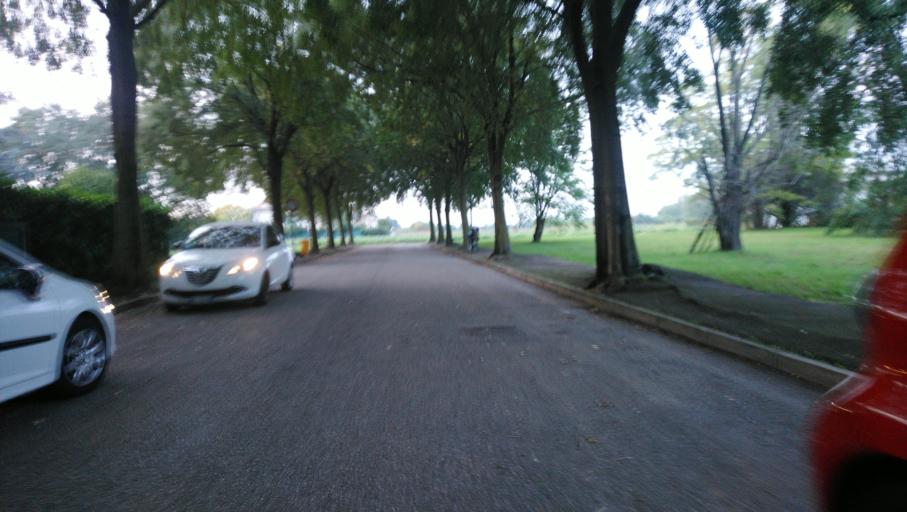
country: IT
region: Veneto
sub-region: Provincia di Treviso
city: Ponzano
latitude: 45.6976
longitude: 12.2274
